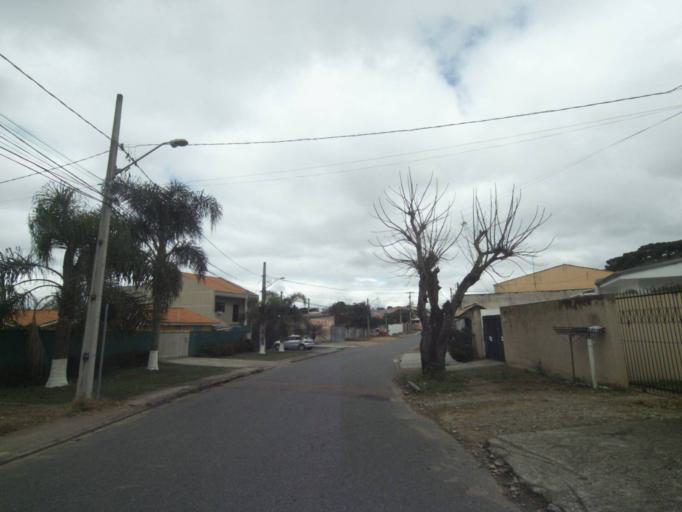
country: BR
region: Parana
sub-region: Sao Jose Dos Pinhais
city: Sao Jose dos Pinhais
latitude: -25.5360
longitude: -49.2859
